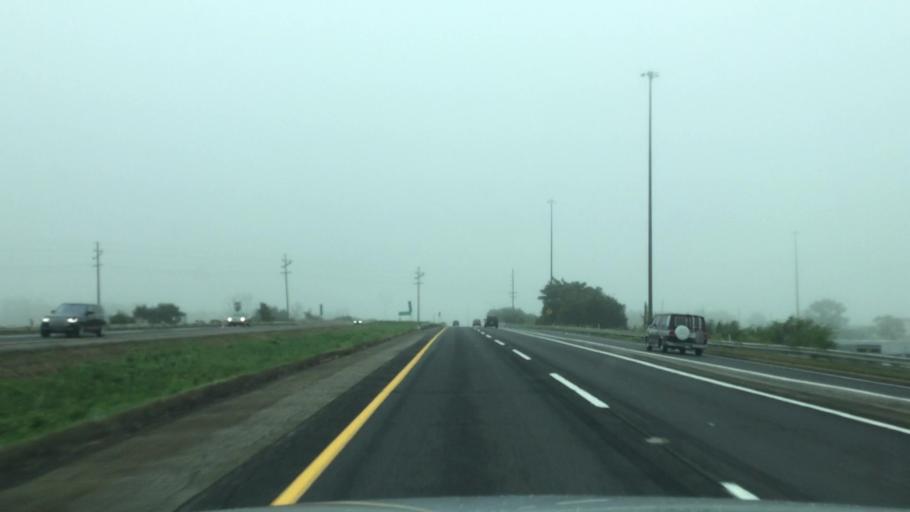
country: US
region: Illinois
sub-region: Cook County
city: Calumet City
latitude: 41.6465
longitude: -87.5104
